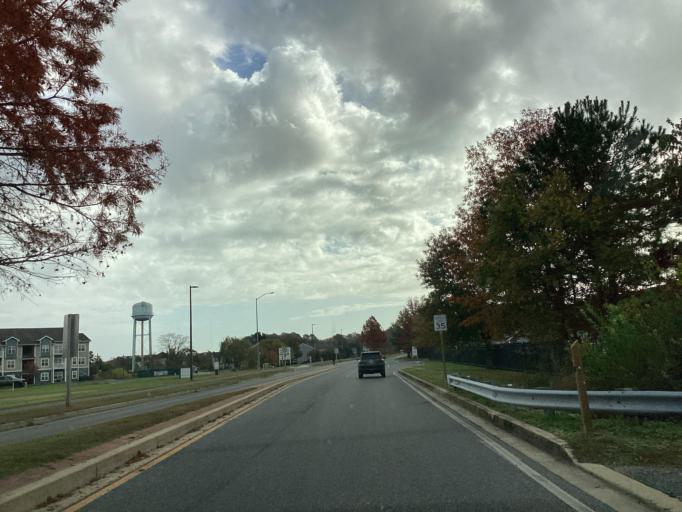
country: US
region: Maryland
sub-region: Somerset County
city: Princess Anne
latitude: 38.2190
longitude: -75.6946
